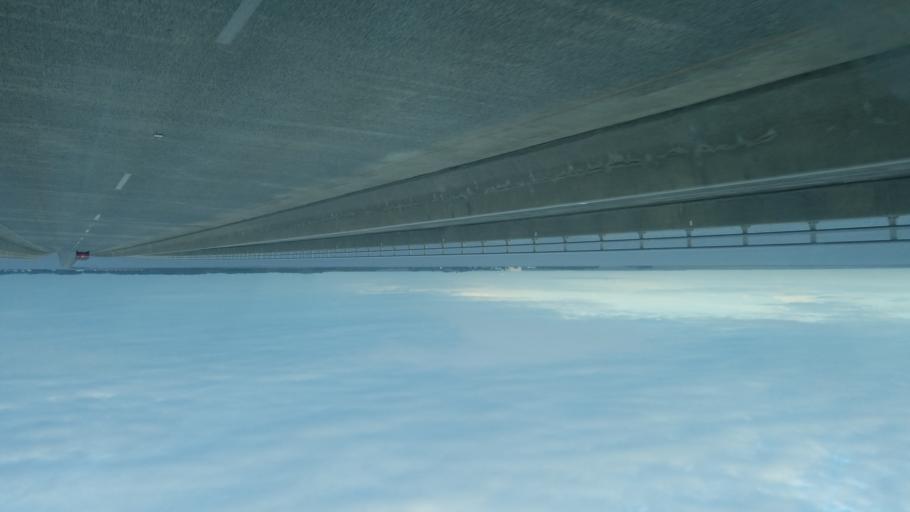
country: US
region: North Carolina
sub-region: Dare County
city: Manteo
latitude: 35.8857
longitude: -75.7186
